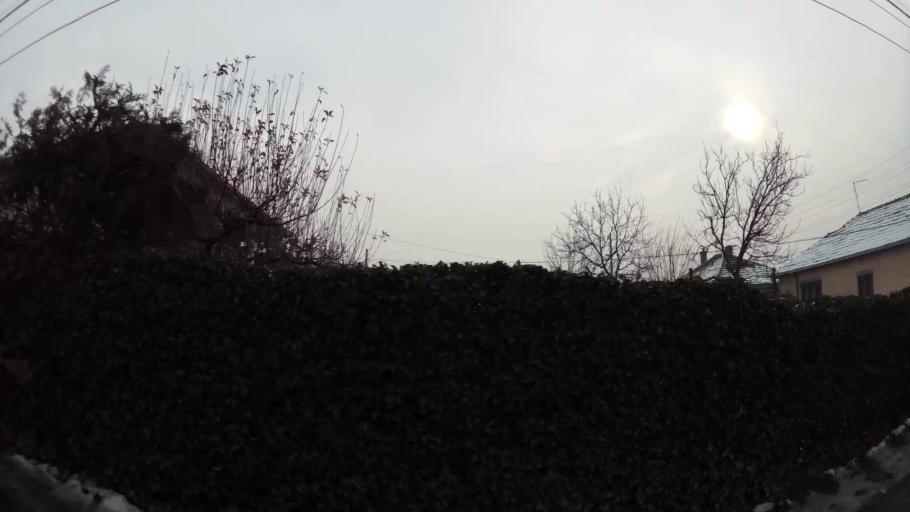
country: MK
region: Ilinden
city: Jurumleri
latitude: 41.9669
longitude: 21.5611
